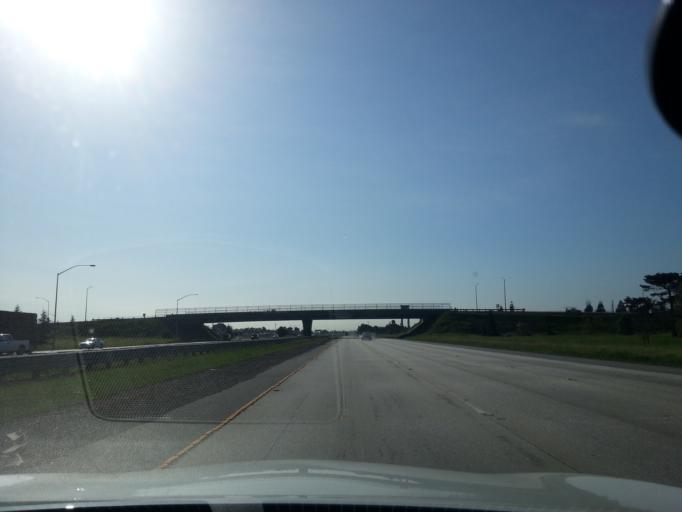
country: US
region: California
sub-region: Santa Clara County
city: Morgan Hill
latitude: 37.1331
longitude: -121.6346
